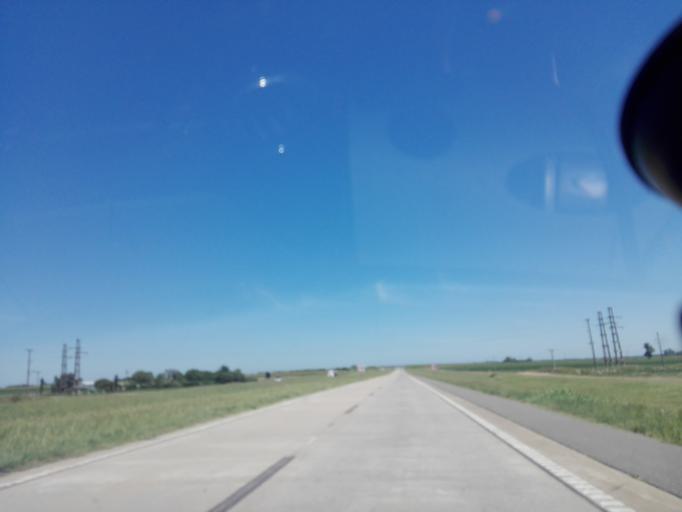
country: AR
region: Santa Fe
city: Carcarana
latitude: -32.8821
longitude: -61.1369
